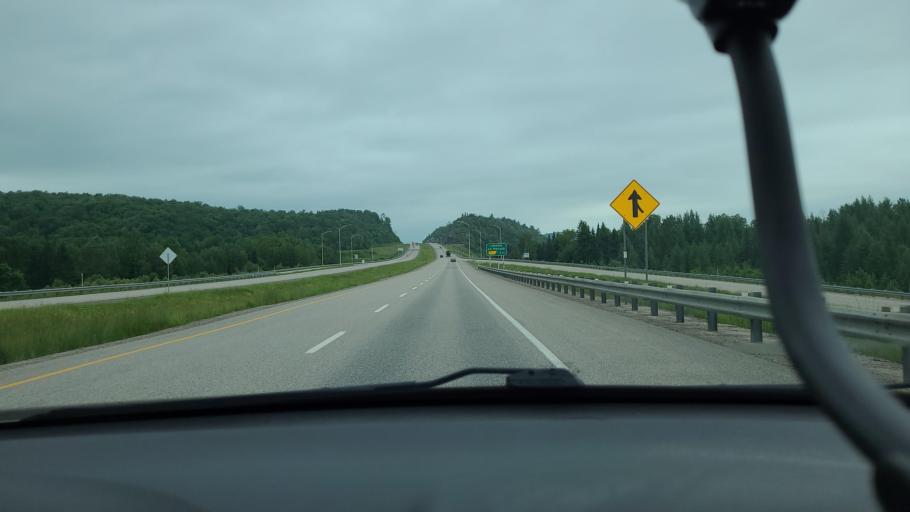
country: CA
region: Quebec
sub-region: Laurentides
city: Labelle
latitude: 46.2579
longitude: -74.7249
